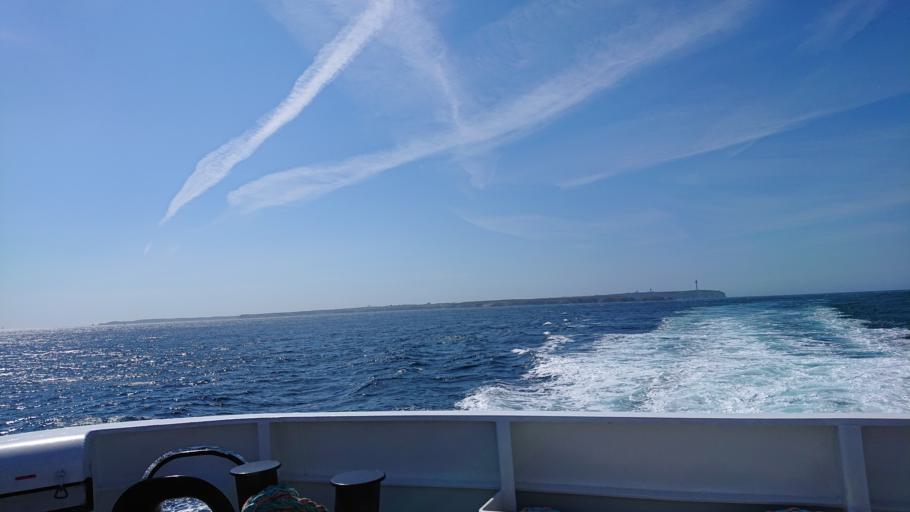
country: FR
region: Brittany
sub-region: Departement du Finistere
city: Porspoder
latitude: 48.4496
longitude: -5.0048
